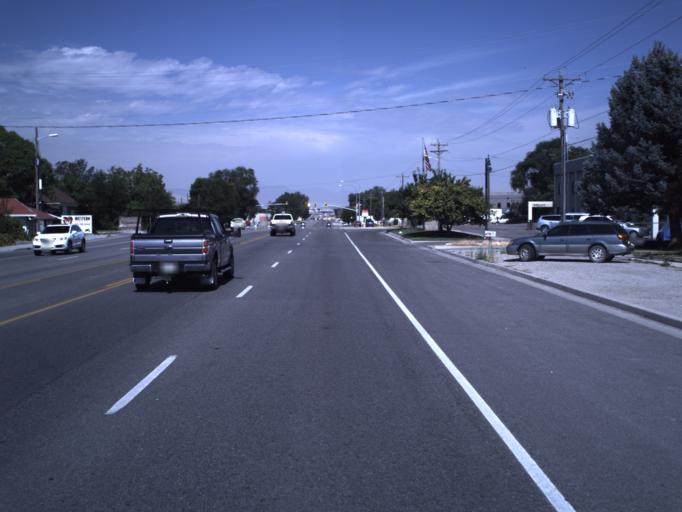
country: US
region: Utah
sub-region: Utah County
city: Lehi
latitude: 40.4047
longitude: -111.8582
